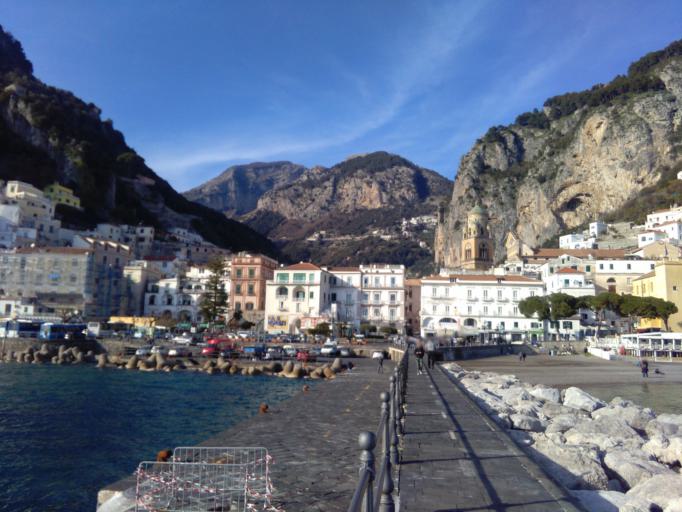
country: IT
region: Campania
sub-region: Provincia di Salerno
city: Amalfi
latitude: 40.6326
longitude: 14.6031
